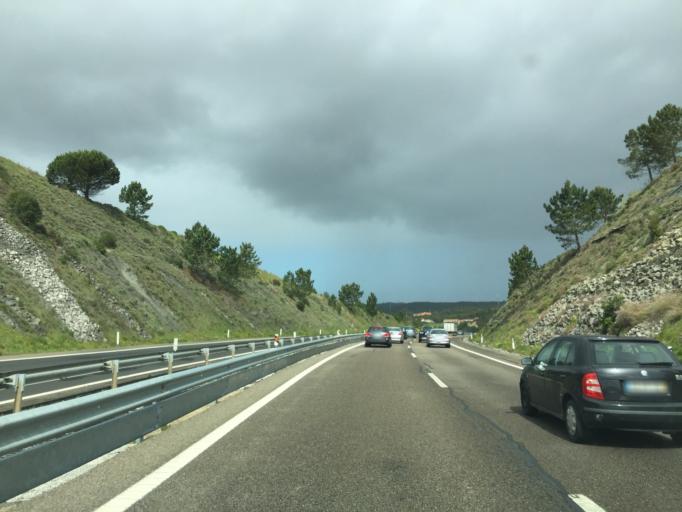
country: PT
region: Lisbon
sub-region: Torres Vedras
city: Torres Vedras
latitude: 39.0961
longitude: -9.2397
